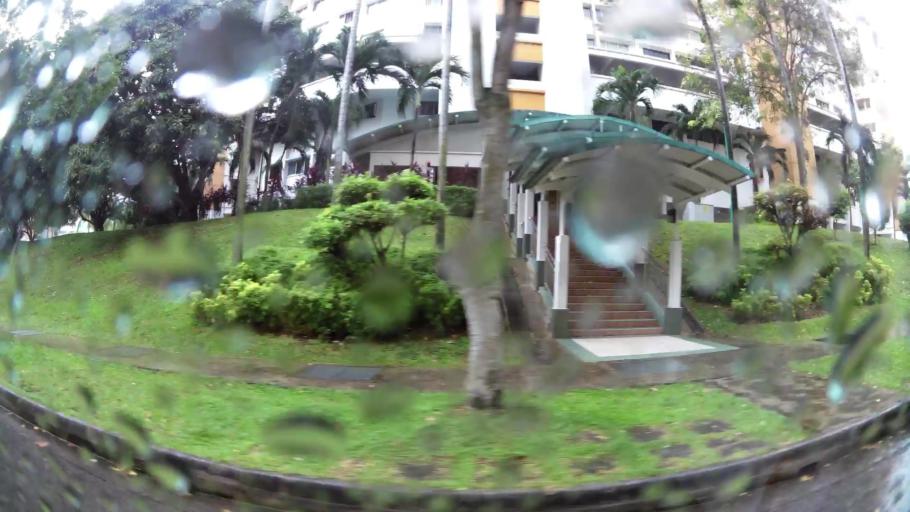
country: SG
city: Singapore
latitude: 1.3359
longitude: 103.8815
